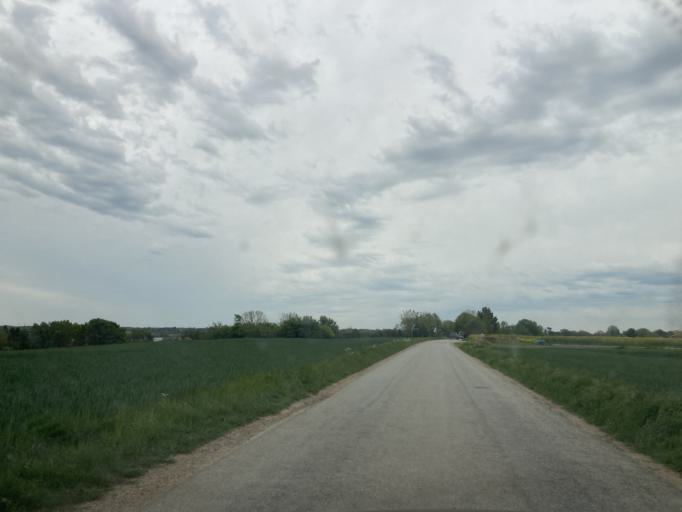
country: DK
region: Zealand
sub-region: Roskilde Kommune
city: Svogerslev
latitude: 55.6687
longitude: 12.0031
